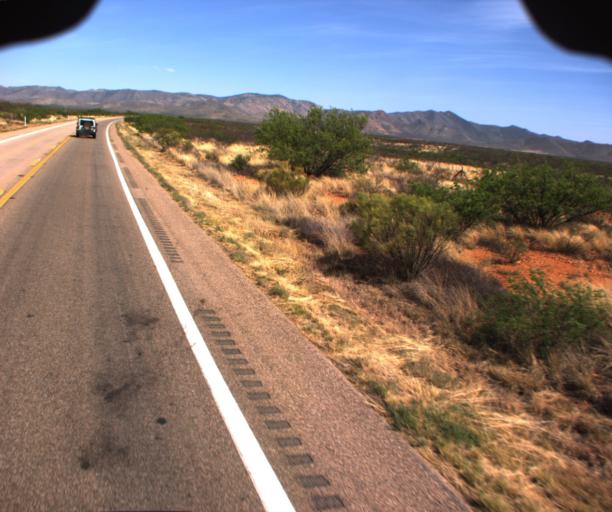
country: US
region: Arizona
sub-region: Cochise County
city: Sierra Vista Southeast
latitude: 31.5425
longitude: -110.0805
